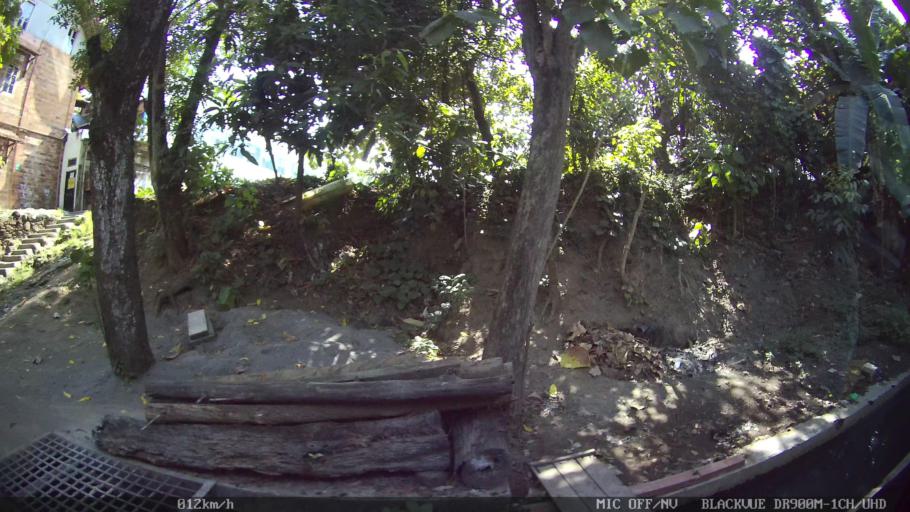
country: ID
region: Daerah Istimewa Yogyakarta
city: Sewon
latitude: -7.8356
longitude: 110.3945
